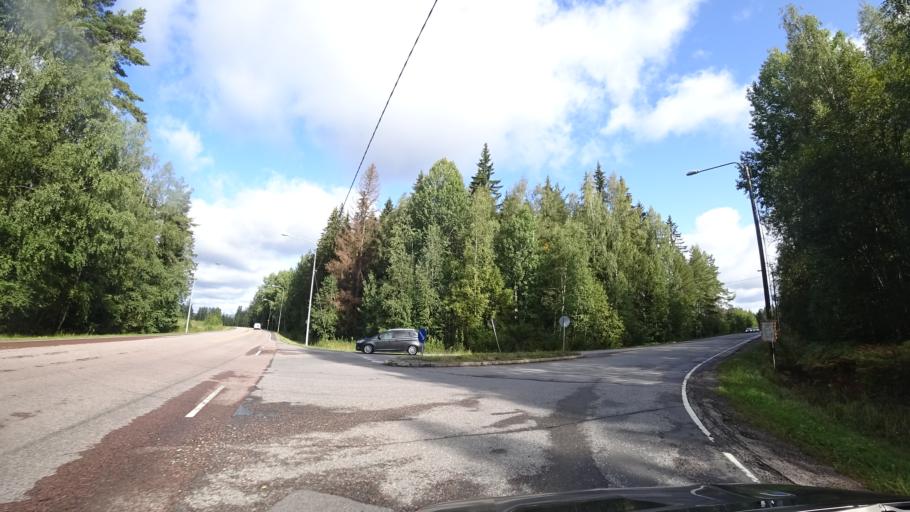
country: FI
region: Uusimaa
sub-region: Helsinki
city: Hyvinge
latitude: 60.5333
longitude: 24.9187
